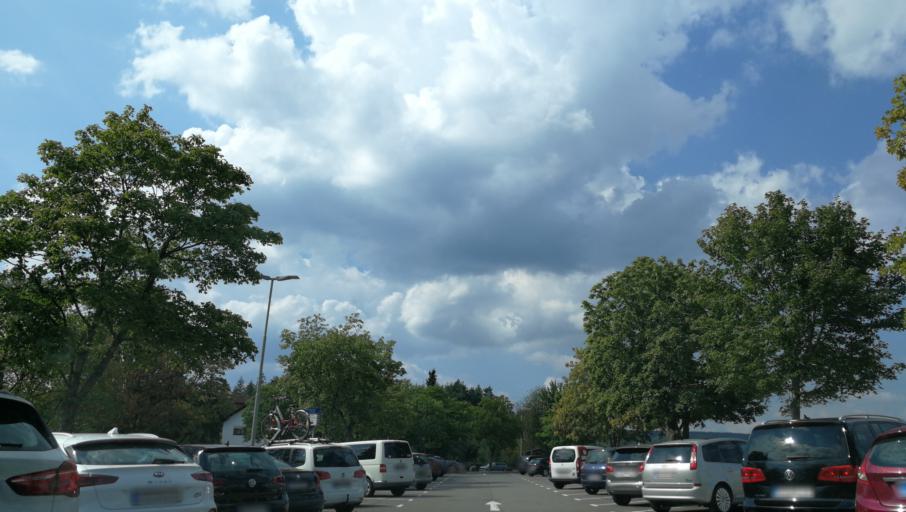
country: DE
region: Saarland
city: Losheim
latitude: 49.5208
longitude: 6.7401
